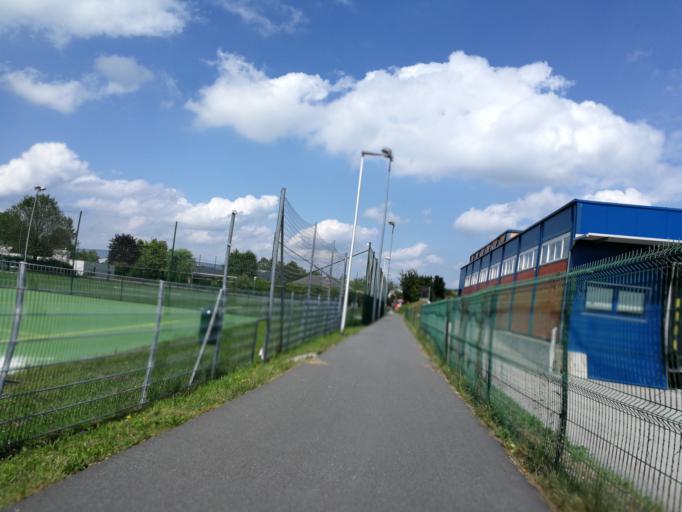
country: DE
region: Bavaria
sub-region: Upper Bavaria
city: Freilassing
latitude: 47.8097
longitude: 12.9891
